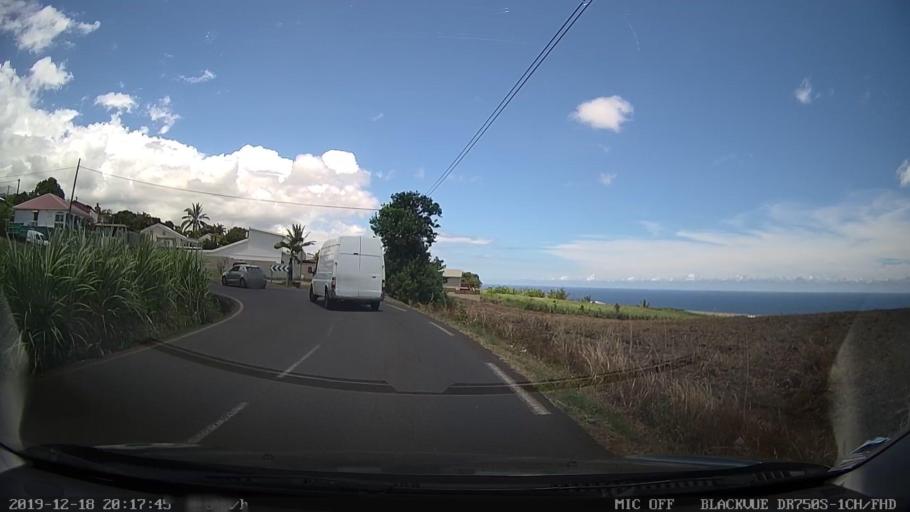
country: RE
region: Reunion
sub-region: Reunion
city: Sainte-Marie
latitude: -20.9214
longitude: 55.5387
